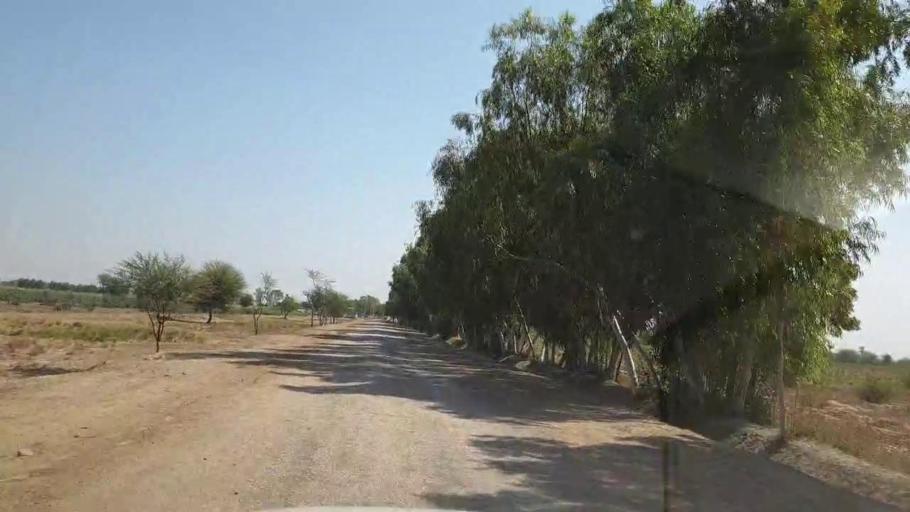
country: PK
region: Sindh
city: Kunri
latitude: 25.1136
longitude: 69.5354
